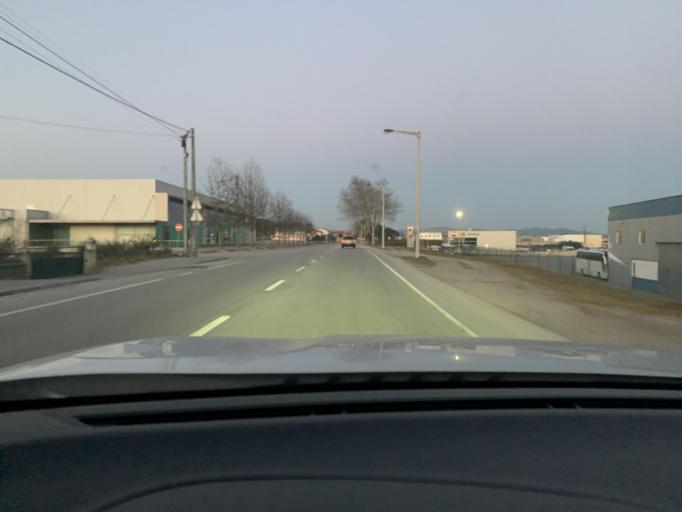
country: PT
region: Viseu
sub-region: Viseu
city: Rio de Loba
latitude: 40.6279
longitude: -7.8722
